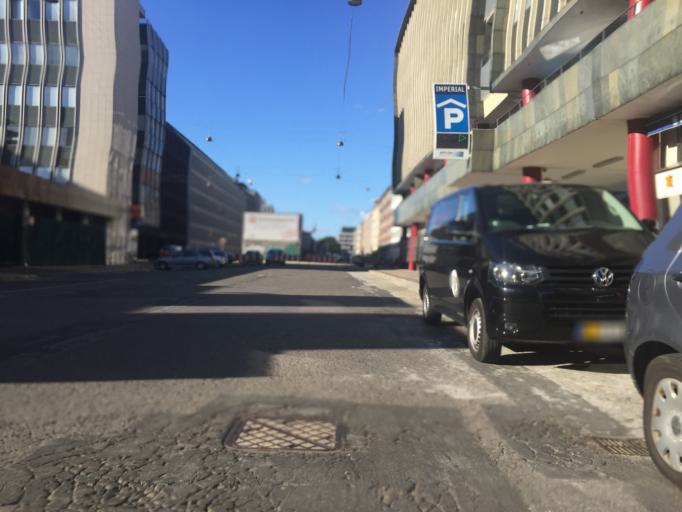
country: DK
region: Capital Region
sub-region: Kobenhavn
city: Copenhagen
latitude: 55.6755
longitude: 12.5604
